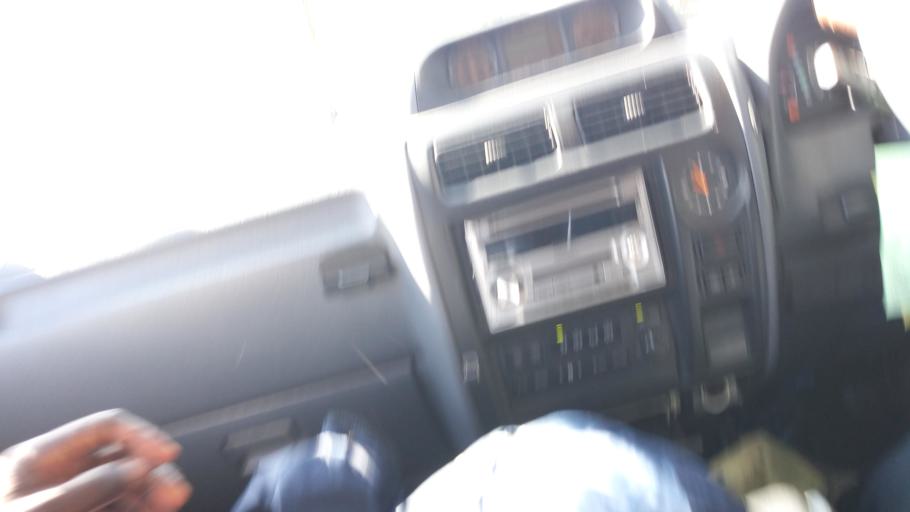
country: UG
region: Northern Region
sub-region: Arua District
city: Arua
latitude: 3.0800
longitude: 31.2842
